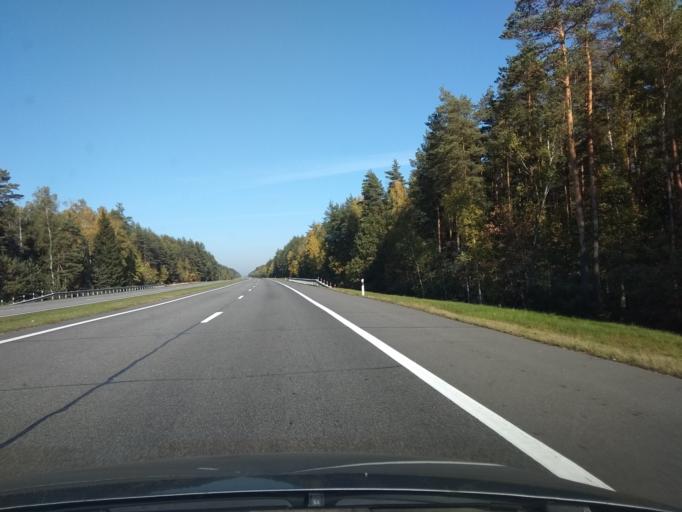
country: BY
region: Grodnenskaya
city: Zhyrovichy
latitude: 52.8632
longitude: 25.6532
